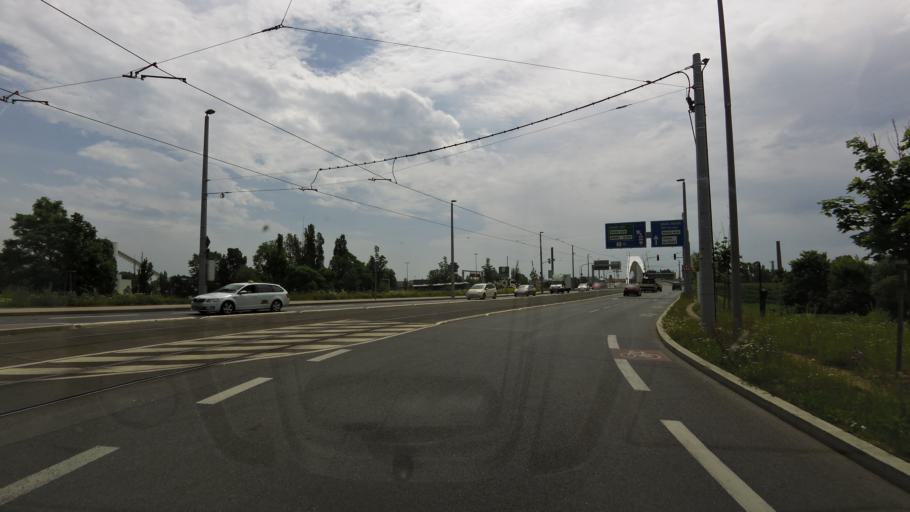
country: CZ
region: Praha
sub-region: Praha 8
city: Karlin
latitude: 50.1157
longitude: 14.4347
